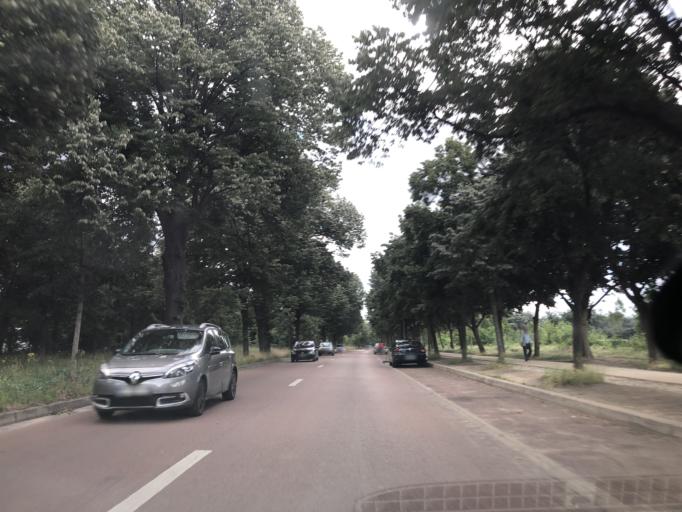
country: FR
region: Ile-de-France
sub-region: Departement du Val-de-Marne
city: Vincennes
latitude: 48.8329
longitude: 2.4466
